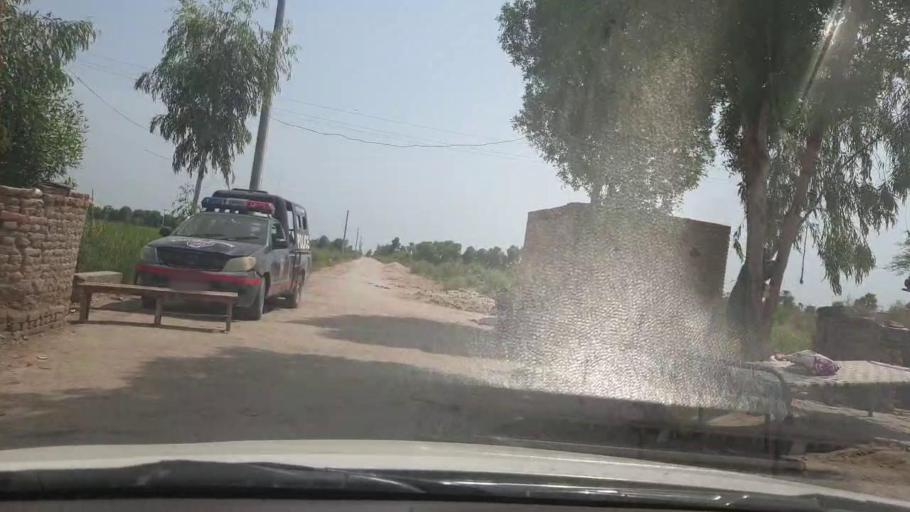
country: PK
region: Sindh
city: Garhi Yasin
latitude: 27.9776
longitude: 68.5030
